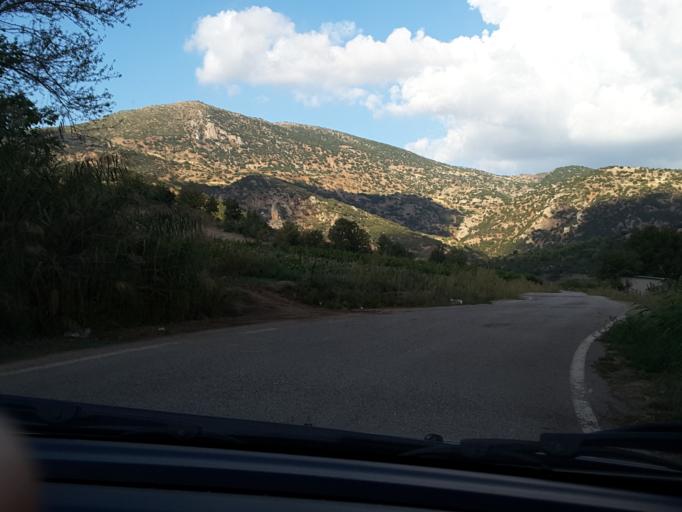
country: GR
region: West Greece
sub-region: Nomos Achaias
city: Kalavryta
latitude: 38.1171
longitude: 22.0870
